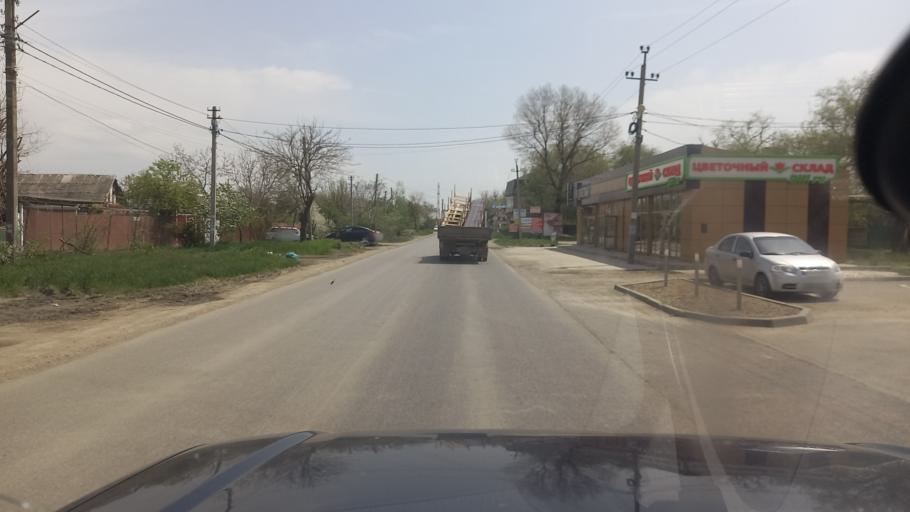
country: RU
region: Adygeya
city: Yablonovskiy
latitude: 44.9870
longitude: 38.9605
